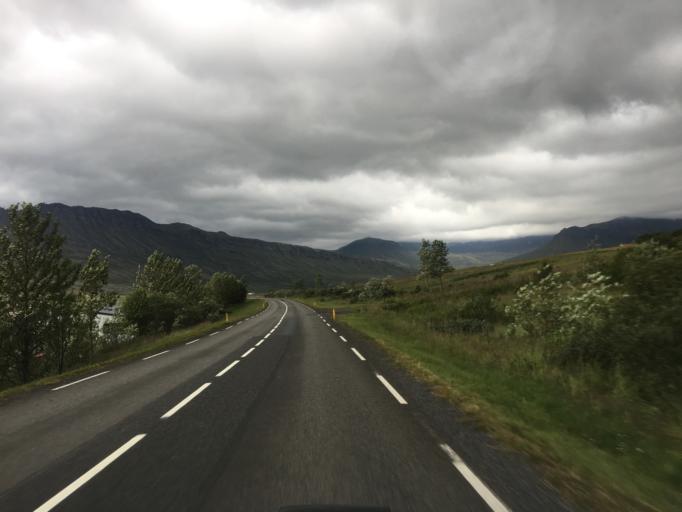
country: IS
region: East
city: Neskaupstadur
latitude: 65.1412
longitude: -13.7407
